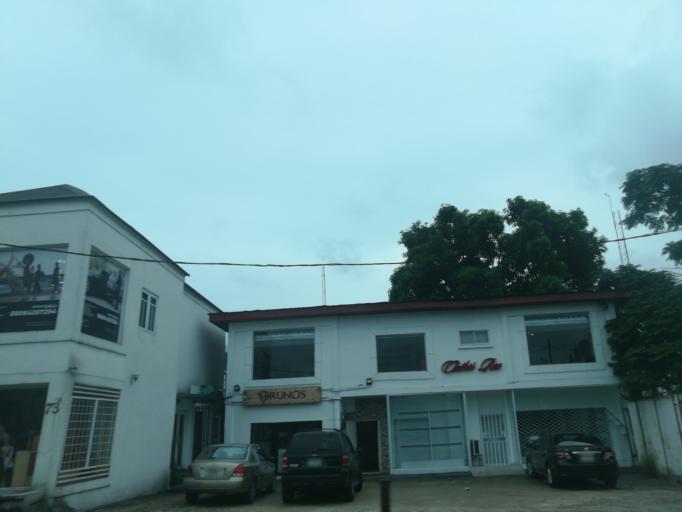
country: NG
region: Rivers
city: Port Harcourt
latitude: 4.8206
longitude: 6.9974
